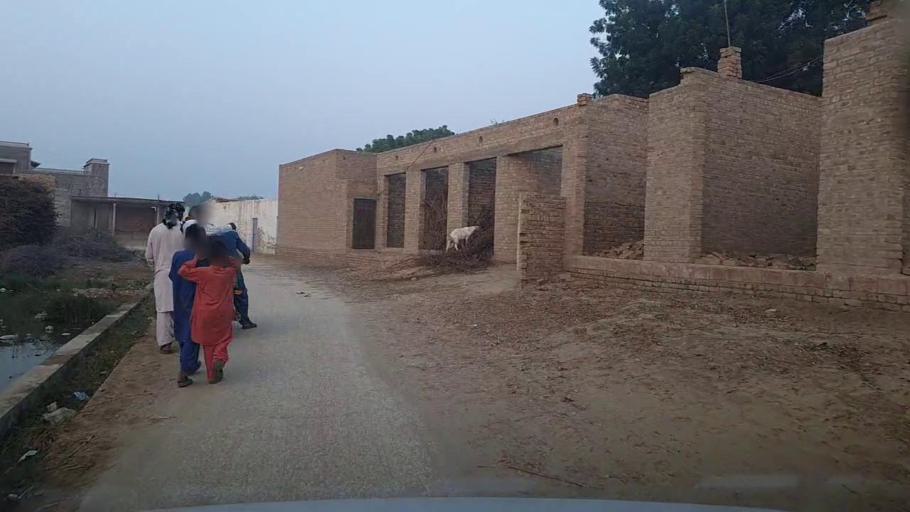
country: PK
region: Sindh
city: Bozdar
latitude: 27.0705
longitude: 68.5983
